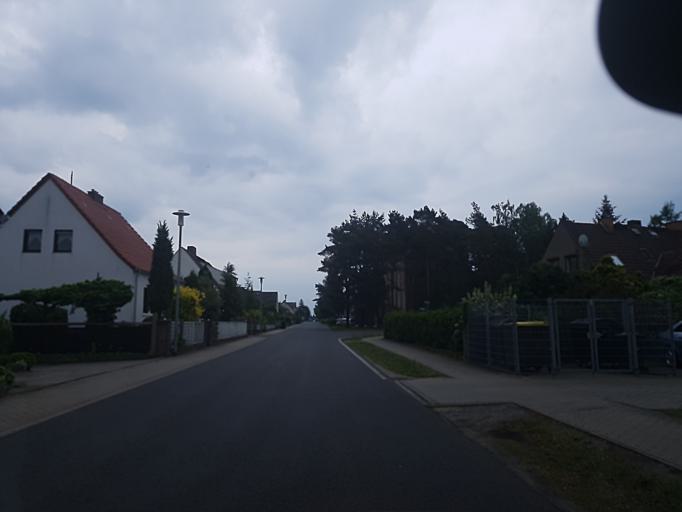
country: DE
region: Saxony-Anhalt
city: Jessen
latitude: 51.7993
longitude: 12.9596
